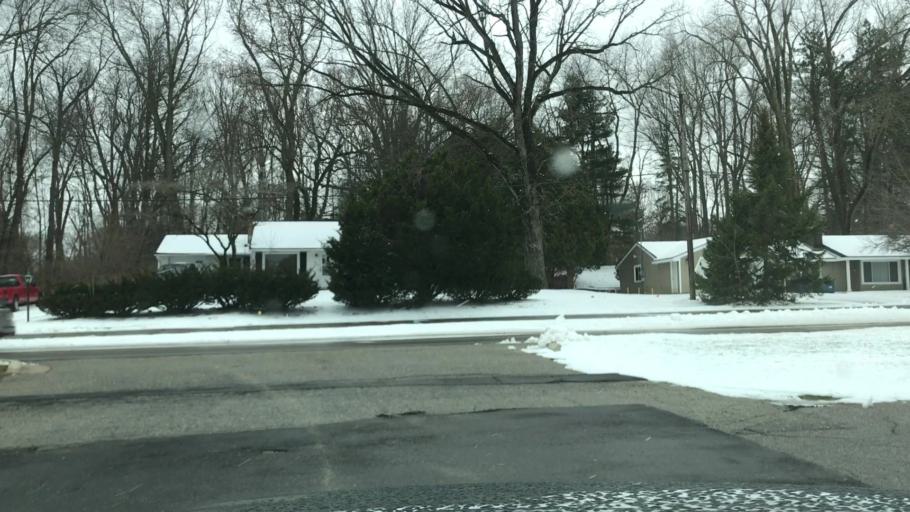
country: US
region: Michigan
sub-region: Kent County
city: Forest Hills
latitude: 42.9207
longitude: -85.5077
